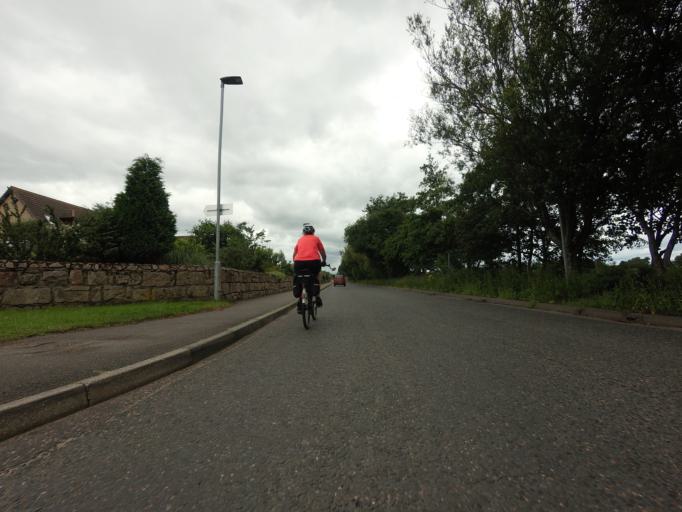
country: GB
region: Scotland
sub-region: Highland
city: Nairn
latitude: 57.5884
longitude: -3.8493
